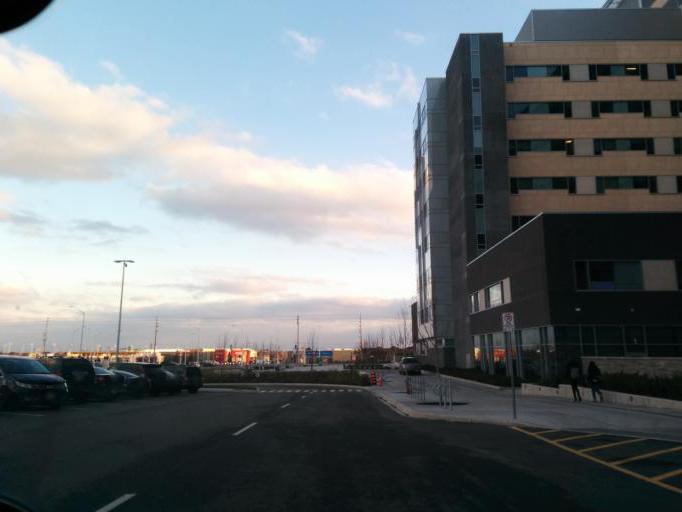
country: CA
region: Ontario
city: Oakville
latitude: 43.4511
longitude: -79.7633
